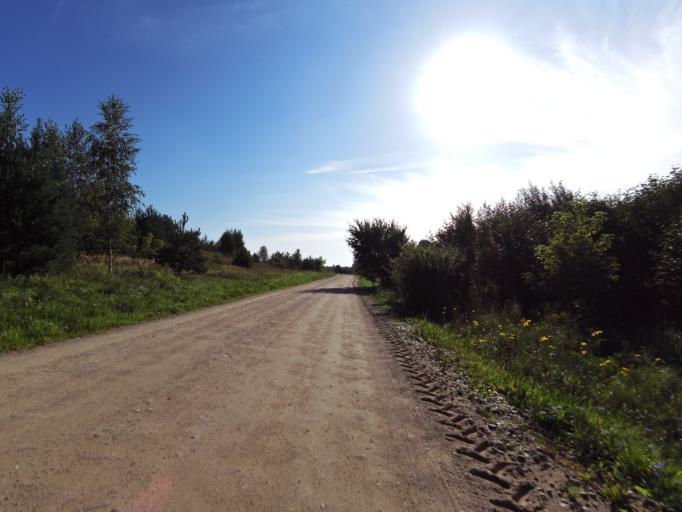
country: LT
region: Vilnius County
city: Pilaite
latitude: 54.7019
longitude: 25.1327
